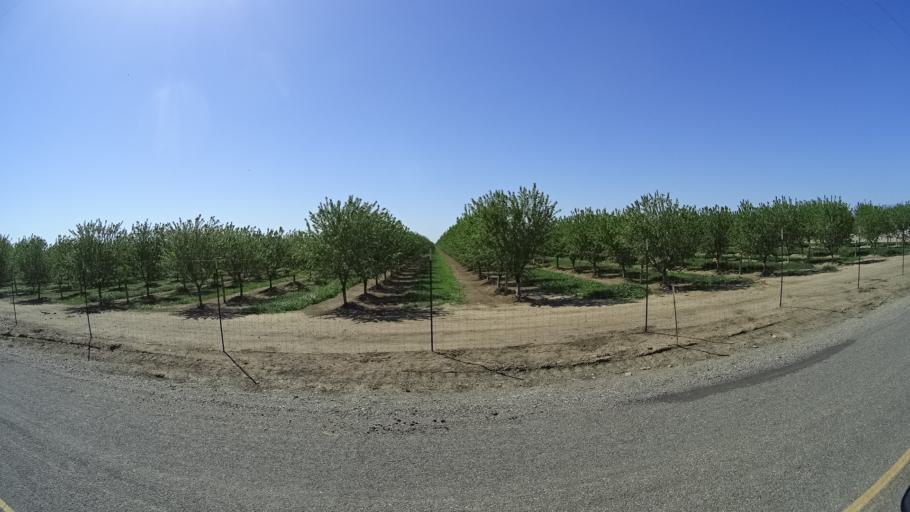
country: US
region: California
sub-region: Glenn County
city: Orland
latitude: 39.6972
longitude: -122.2281
